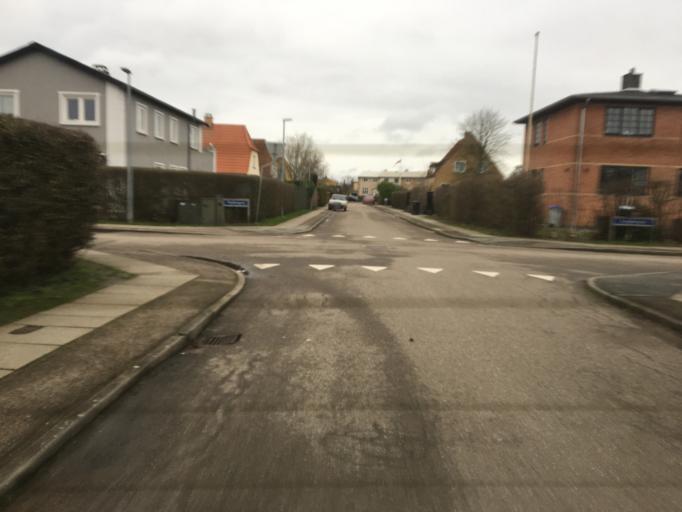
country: DK
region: Capital Region
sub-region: Tarnby Kommune
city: Tarnby
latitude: 55.6206
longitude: 12.6195
